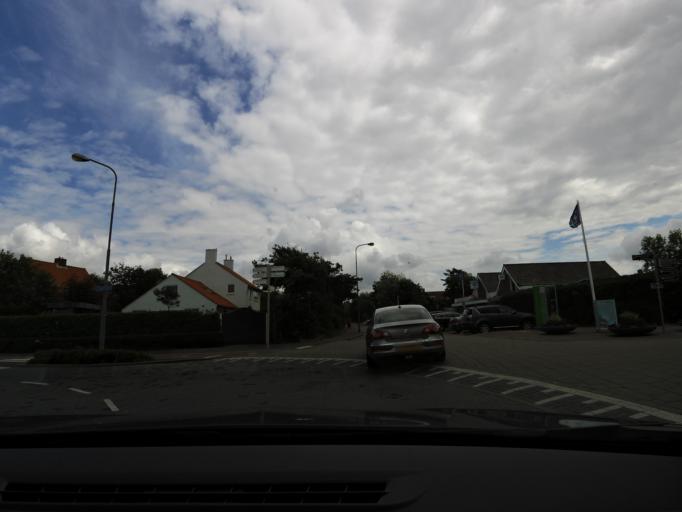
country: NL
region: Zeeland
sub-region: Gemeente Vlissingen
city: Vlissingen
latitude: 51.5010
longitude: 3.4868
